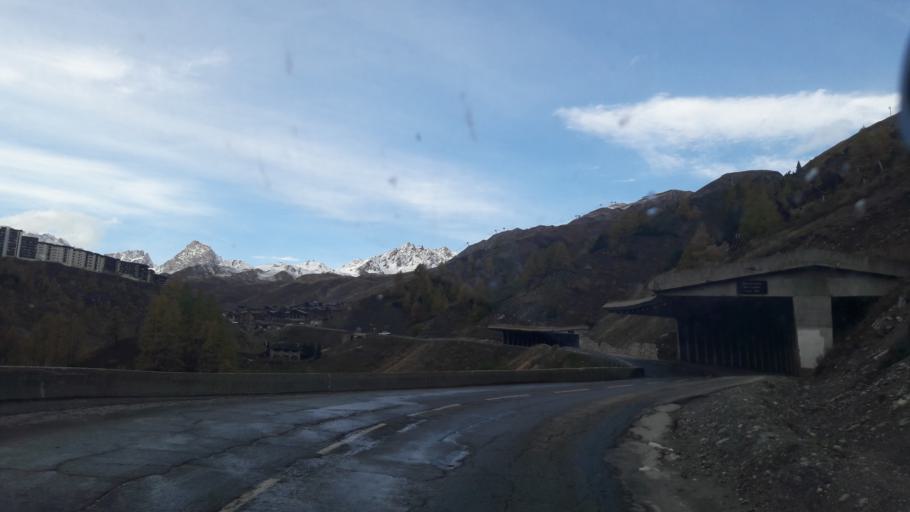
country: FR
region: Rhone-Alpes
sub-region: Departement de la Savoie
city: Tignes
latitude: 45.4778
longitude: 6.9226
